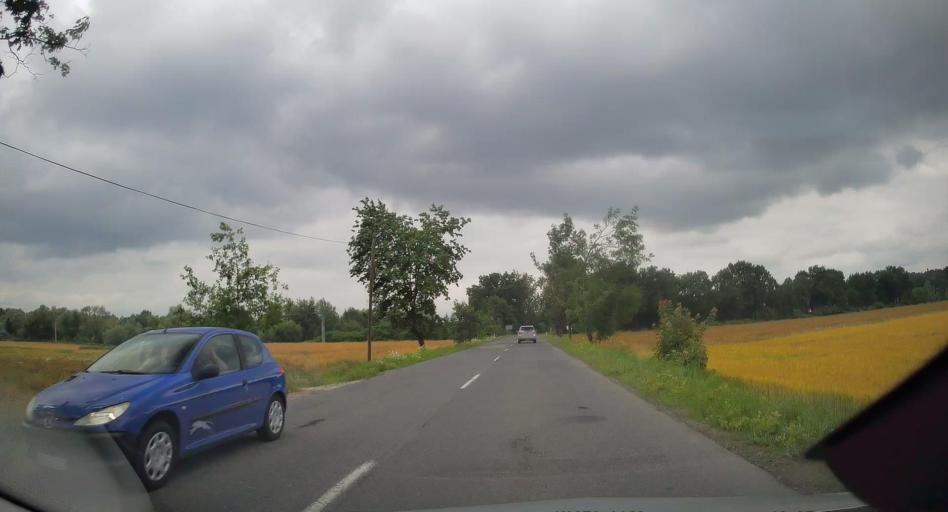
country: PL
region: Opole Voivodeship
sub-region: Powiat nyski
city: Paczkow
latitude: 50.4738
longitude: 17.0084
